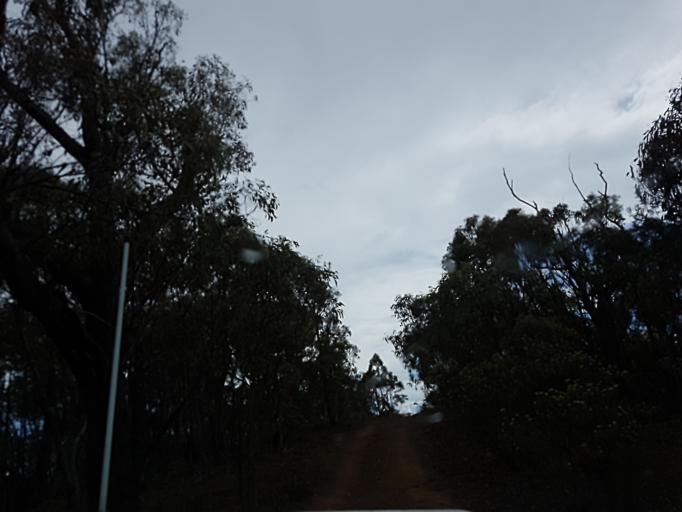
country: AU
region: New South Wales
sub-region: Snowy River
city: Jindabyne
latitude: -36.9077
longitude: 148.3398
